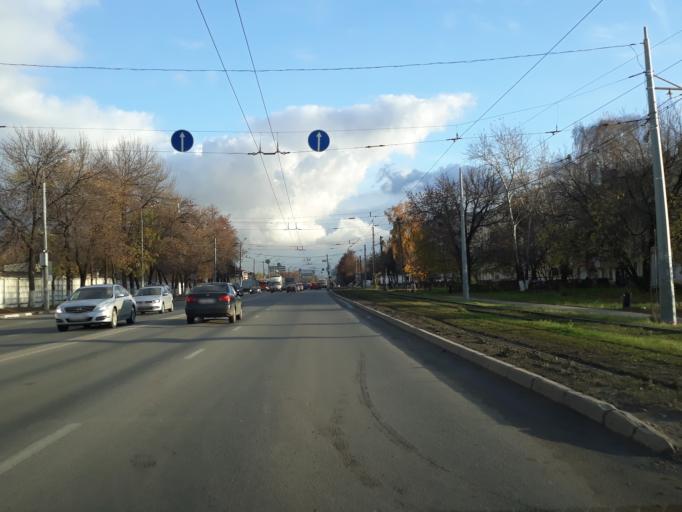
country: RU
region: Nizjnij Novgorod
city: Neklyudovo
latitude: 56.3428
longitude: 43.8760
